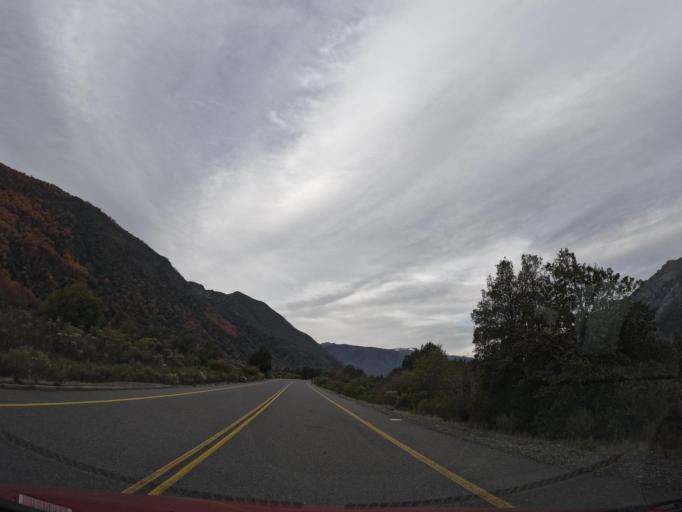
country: CL
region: Maule
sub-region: Provincia de Linares
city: Colbun
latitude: -35.7130
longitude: -71.0581
